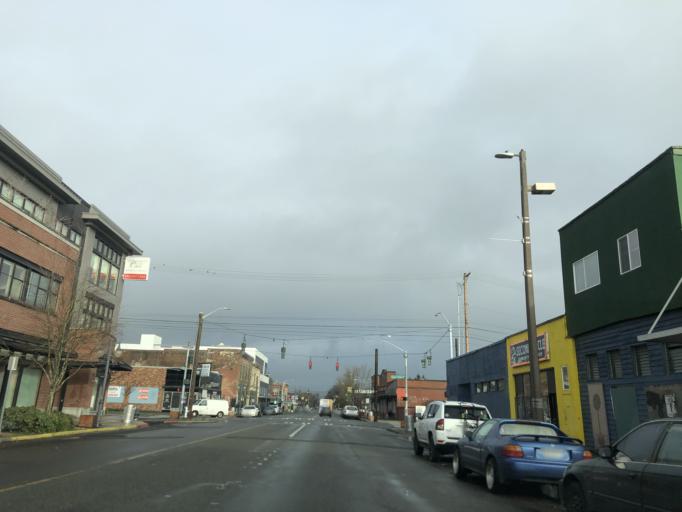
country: US
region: Washington
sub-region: Pierce County
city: Tacoma
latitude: 47.2504
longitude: -122.4513
